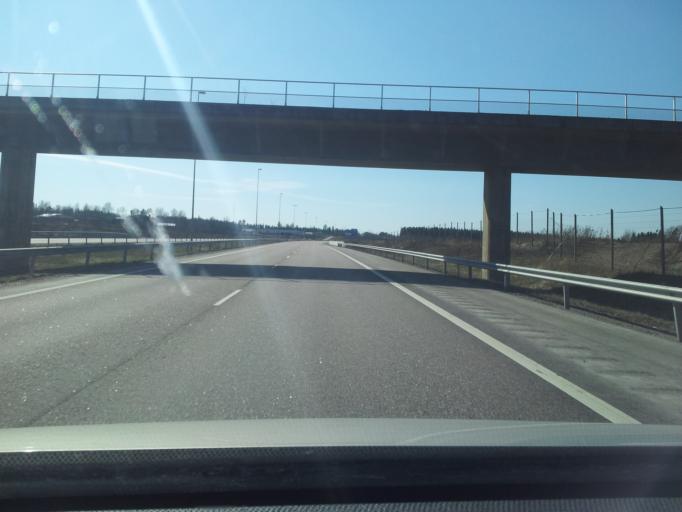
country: FI
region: Uusimaa
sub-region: Loviisa
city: Lovisa
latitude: 60.4645
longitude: 26.2080
